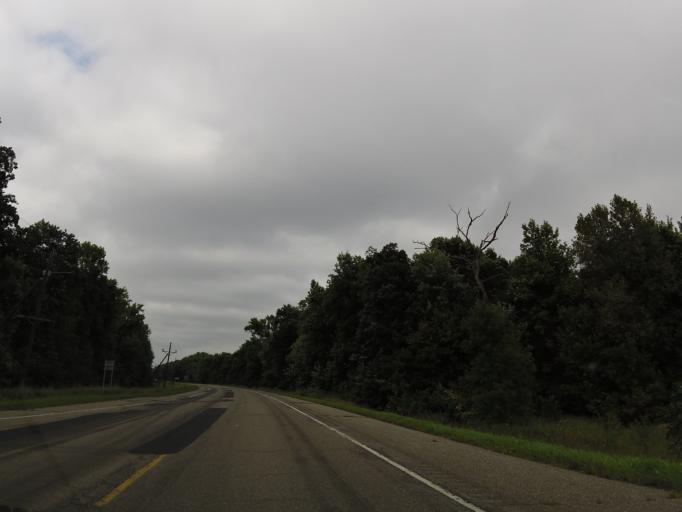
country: US
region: Minnesota
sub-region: Chippewa County
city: Montevideo
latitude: 44.8879
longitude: -95.6580
